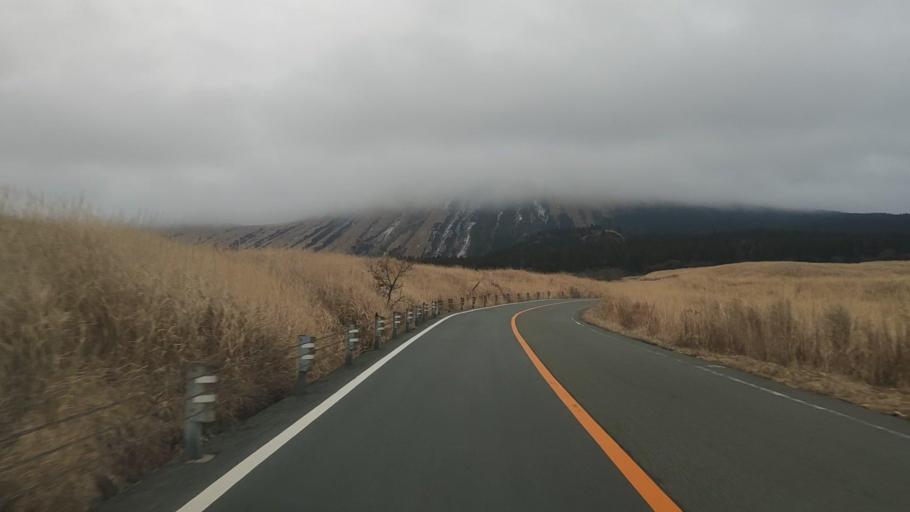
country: JP
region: Kumamoto
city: Aso
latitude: 32.9028
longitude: 131.0400
